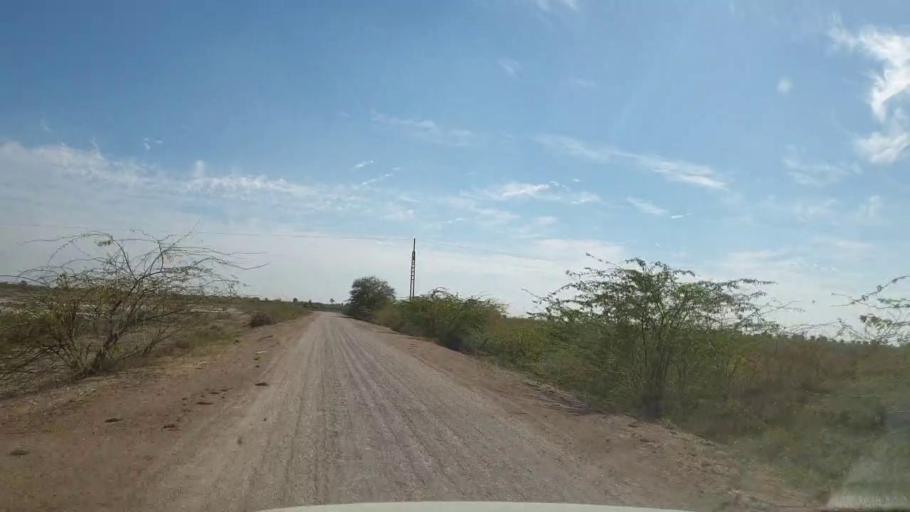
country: PK
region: Sindh
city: Pithoro
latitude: 25.5845
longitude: 69.2880
